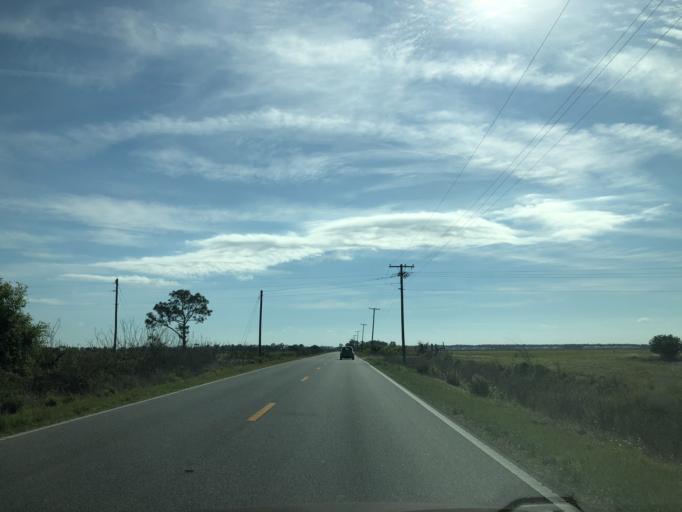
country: US
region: Florida
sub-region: Orange County
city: Tangerine
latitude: 28.7315
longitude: -81.6636
